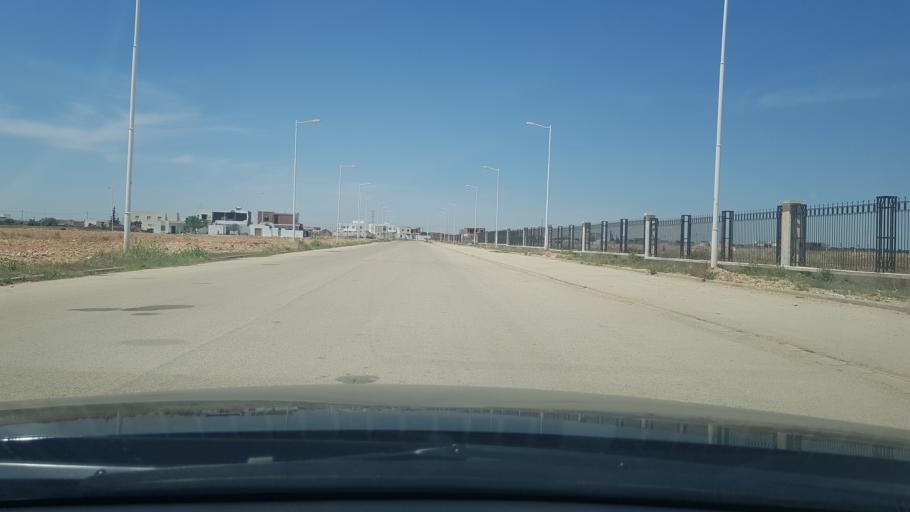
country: TN
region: Safaqis
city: Al Qarmadah
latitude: 34.8338
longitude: 10.7501
